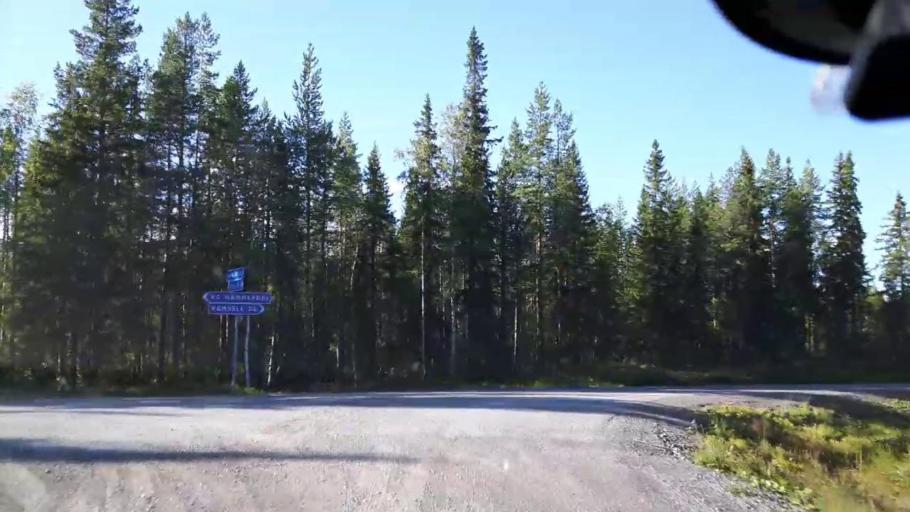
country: SE
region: Jaemtland
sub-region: Ragunda Kommun
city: Hammarstrand
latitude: 63.5356
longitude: 16.0700
